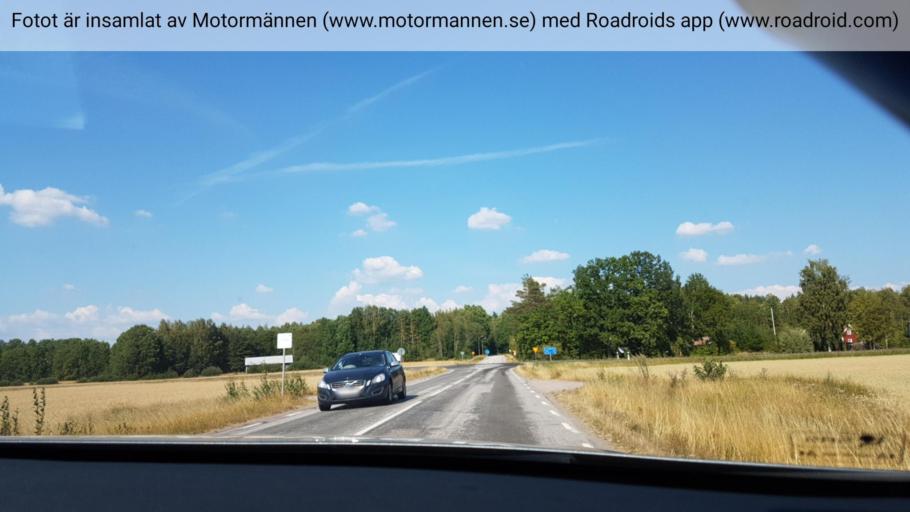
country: SE
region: Vaestra Goetaland
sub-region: Mariestads Kommun
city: Mariestad
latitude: 58.6476
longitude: 13.9027
